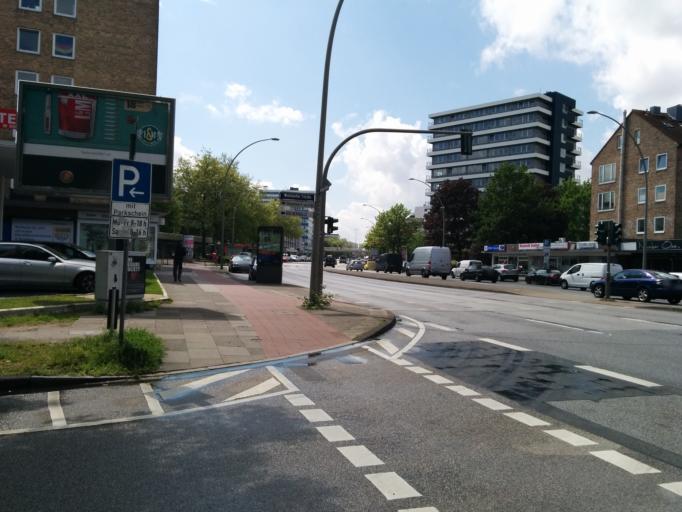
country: DE
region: Hamburg
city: Borgfelde
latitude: 53.5773
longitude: 10.0387
